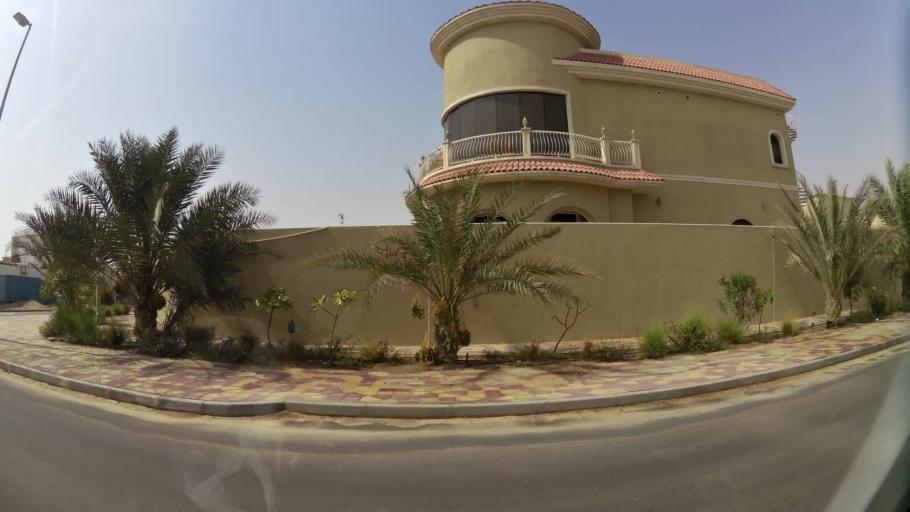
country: AE
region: Ash Shariqah
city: Sharjah
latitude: 25.2566
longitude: 55.4663
